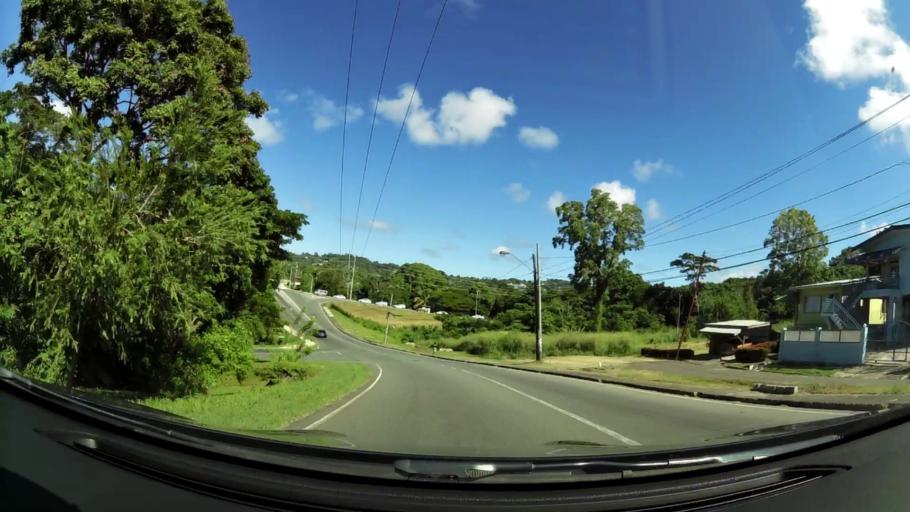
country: TT
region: Tobago
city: Scarborough
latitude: 11.1853
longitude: -60.7317
